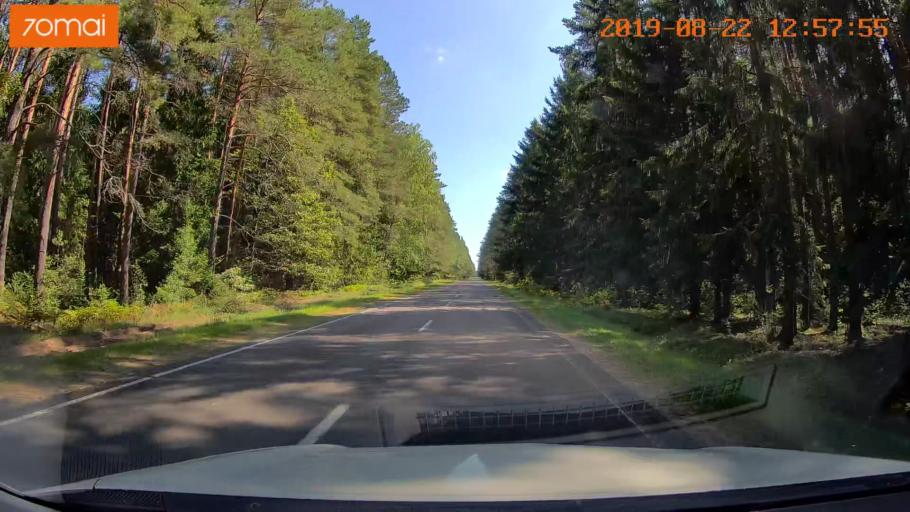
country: BY
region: Minsk
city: Prawdzinski
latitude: 53.4267
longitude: 27.7590
